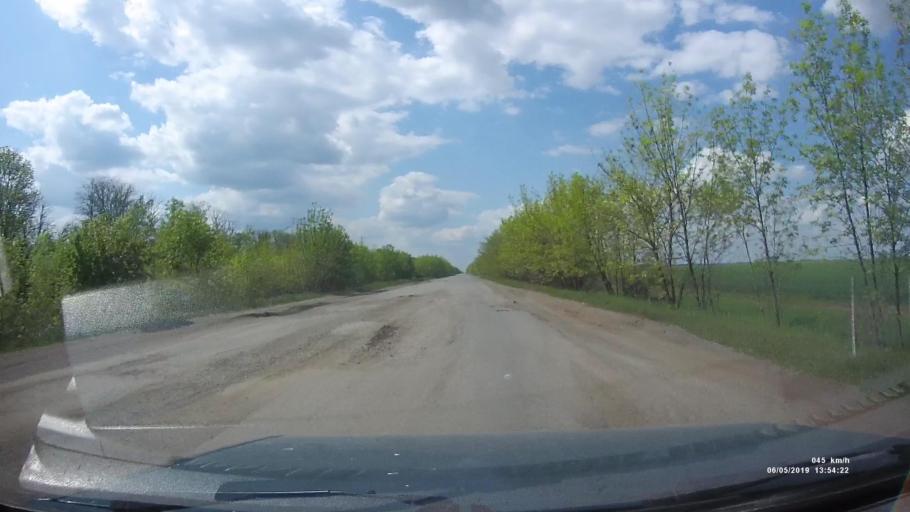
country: RU
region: Rostov
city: Melikhovskaya
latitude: 47.6739
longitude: 40.4487
